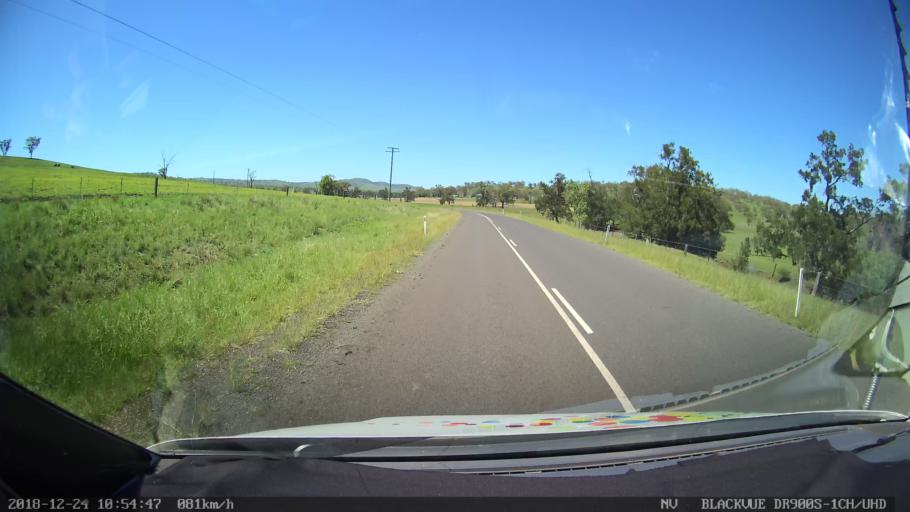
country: AU
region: New South Wales
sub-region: Upper Hunter Shire
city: Merriwa
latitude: -32.0084
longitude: 150.4170
